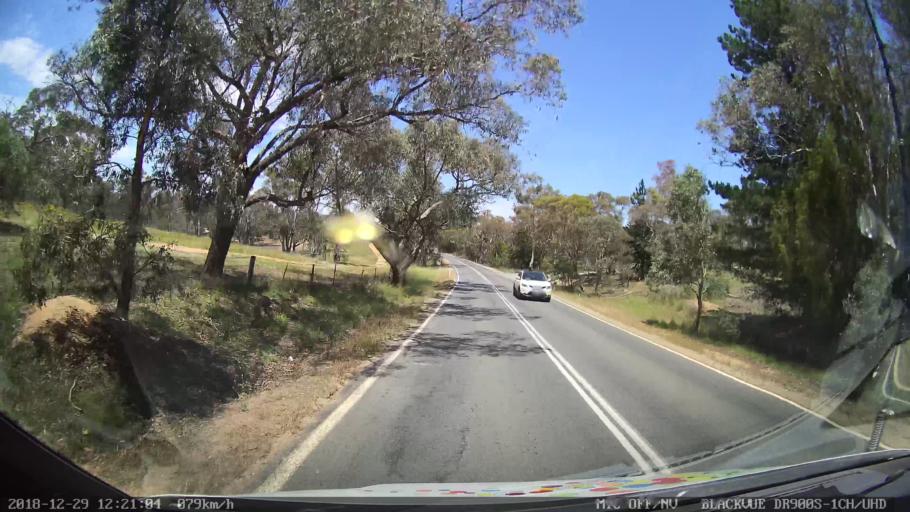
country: AU
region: New South Wales
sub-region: Queanbeyan
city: Queanbeyan
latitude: -35.4096
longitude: 149.2257
